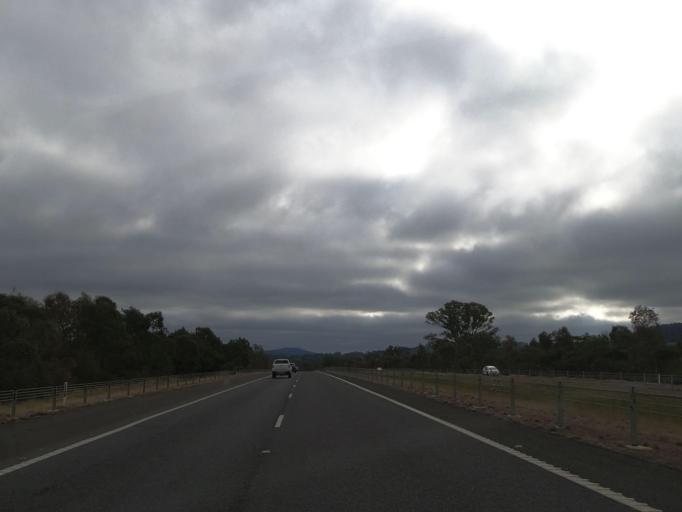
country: AU
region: Victoria
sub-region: Mount Alexander
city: Castlemaine
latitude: -37.0565
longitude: 144.3007
